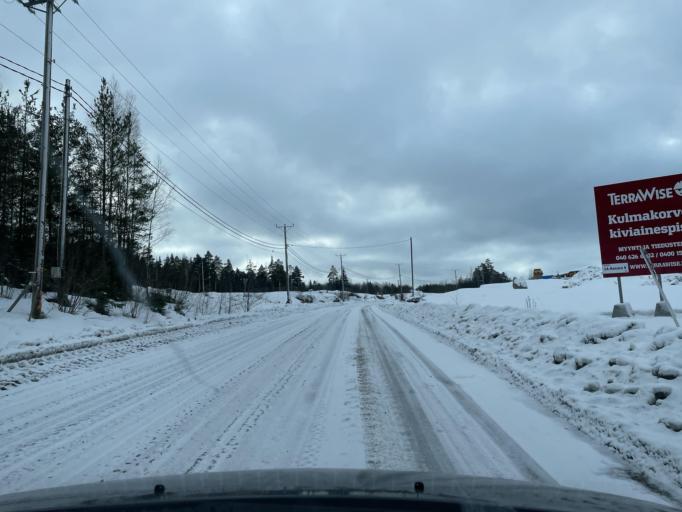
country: FI
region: Uusimaa
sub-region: Helsinki
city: Espoo
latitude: 60.2426
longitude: 24.5602
